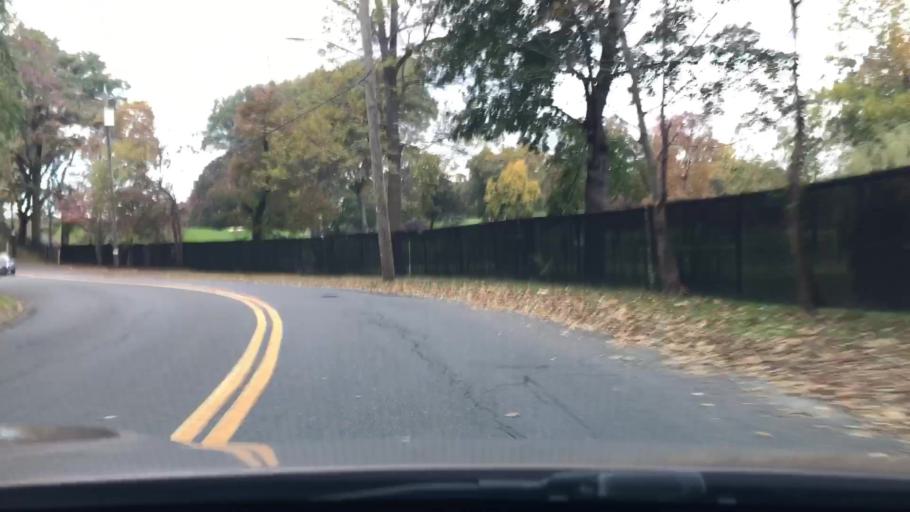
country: US
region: New York
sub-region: Westchester County
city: Tuckahoe
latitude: 40.9661
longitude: -73.8125
